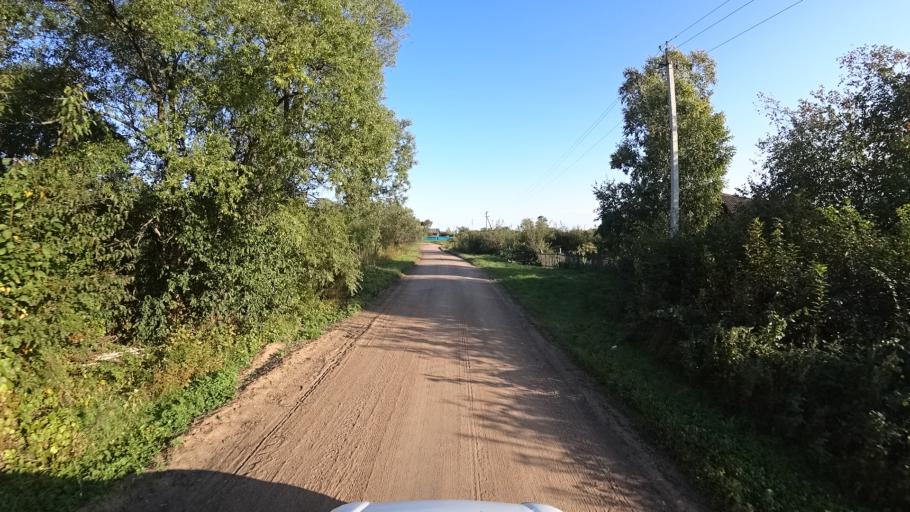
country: RU
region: Amur
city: Arkhara
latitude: 49.3620
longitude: 130.1241
